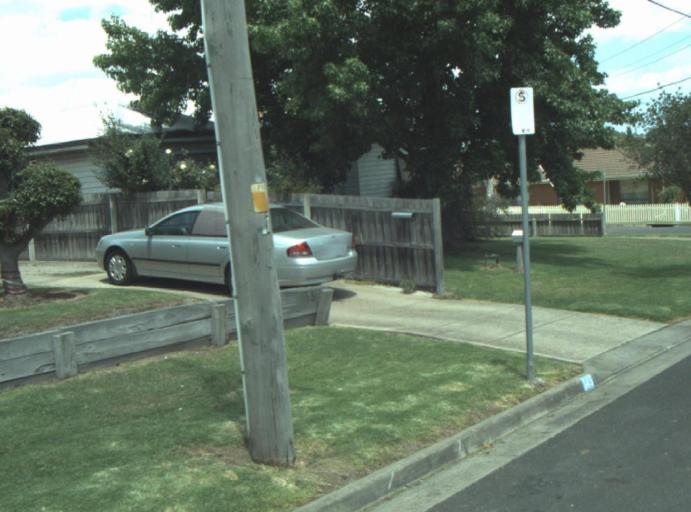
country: AU
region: Victoria
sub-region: Greater Geelong
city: Breakwater
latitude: -38.1855
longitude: 144.3470
